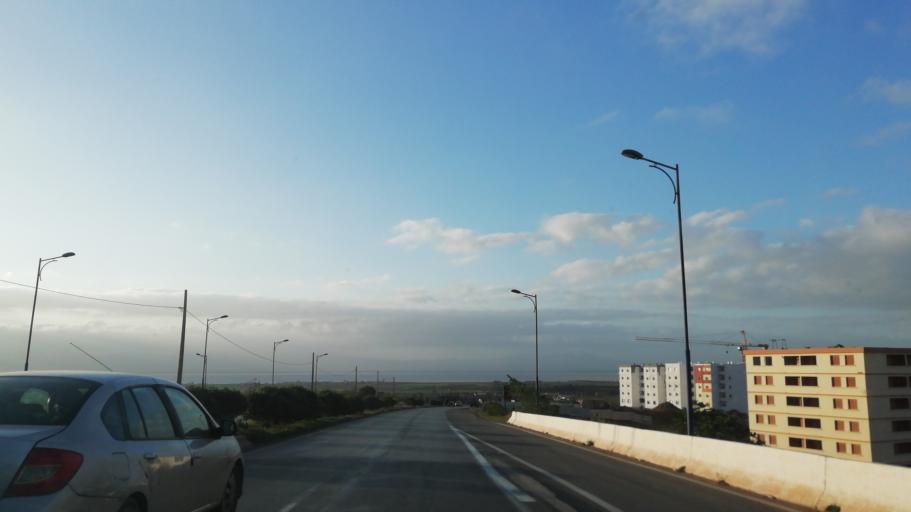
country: DZ
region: Oran
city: Es Senia
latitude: 35.6218
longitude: -0.7185
